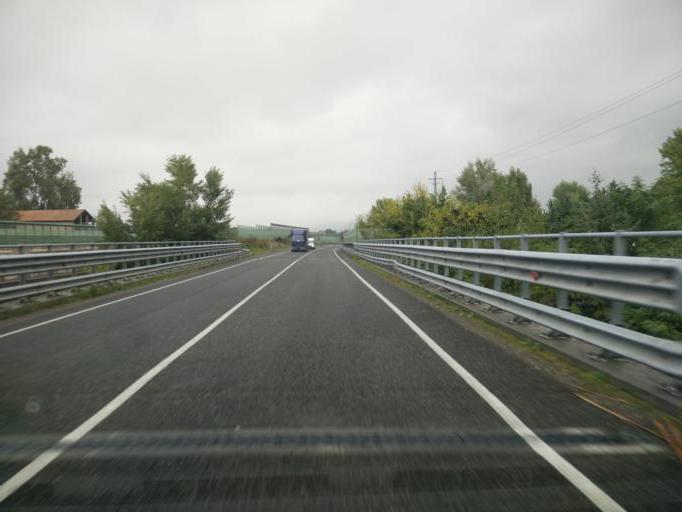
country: IT
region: Emilia-Romagna
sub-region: Provincia di Bologna
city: Borgonuovo
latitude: 44.4153
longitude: 11.2685
